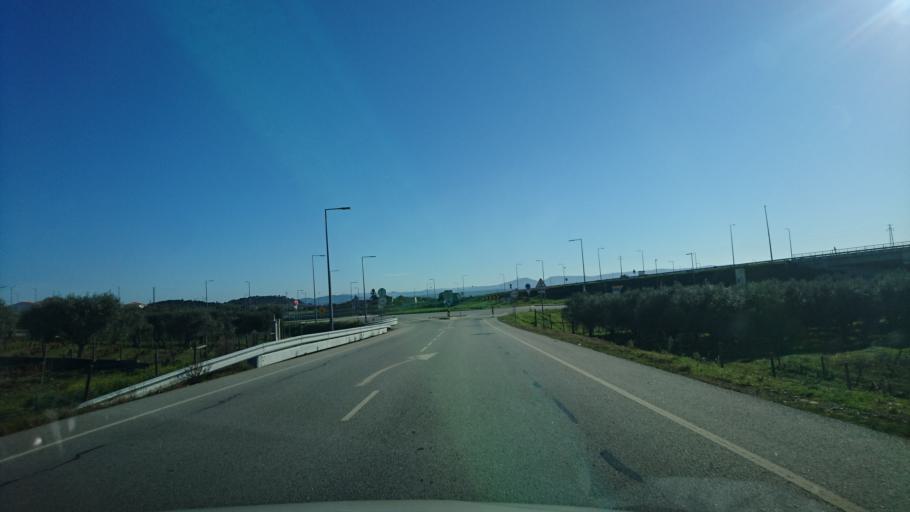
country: PT
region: Braganca
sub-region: Braganca Municipality
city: Vila Flor
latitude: 41.3022
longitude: -7.1583
